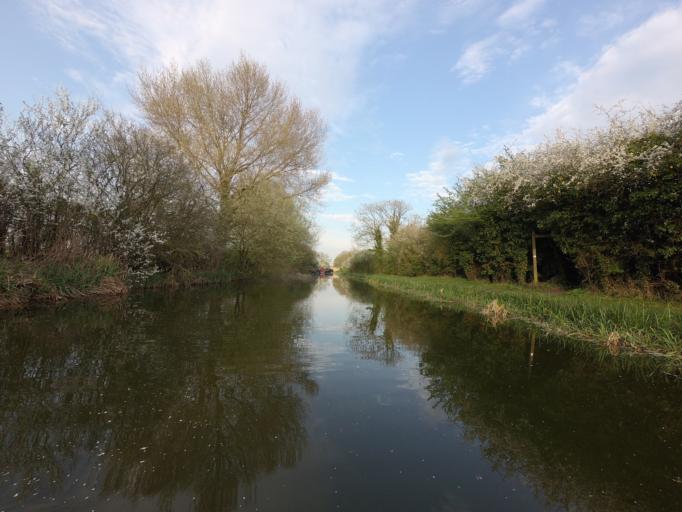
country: GB
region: England
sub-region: Buckinghamshire
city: Aston Clinton
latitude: 51.8174
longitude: -0.7147
